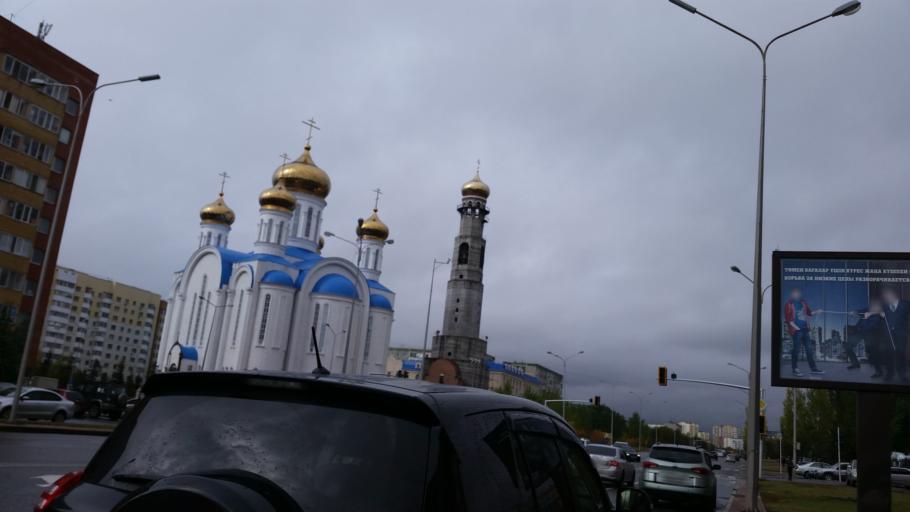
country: KZ
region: Astana Qalasy
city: Astana
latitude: 51.1488
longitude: 71.4834
